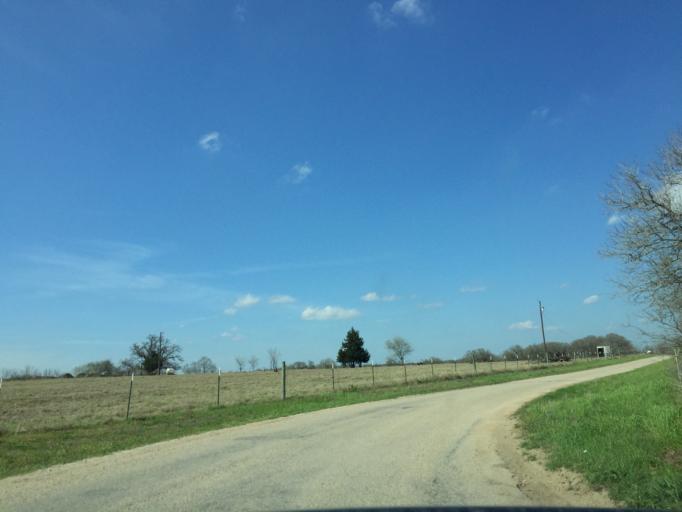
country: US
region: Texas
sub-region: Milam County
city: Thorndale
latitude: 30.5703
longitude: -97.1593
